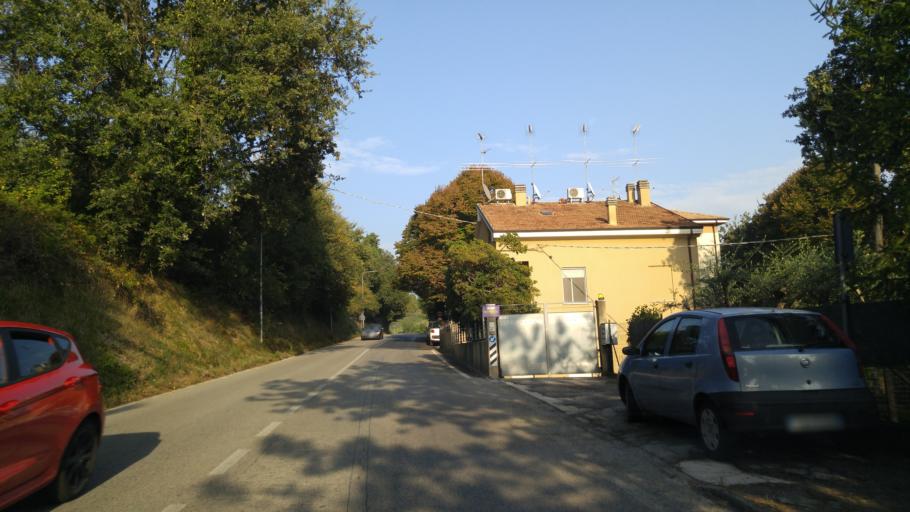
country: IT
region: The Marches
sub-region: Provincia di Pesaro e Urbino
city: Pesaro
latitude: 43.8887
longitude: 12.9391
